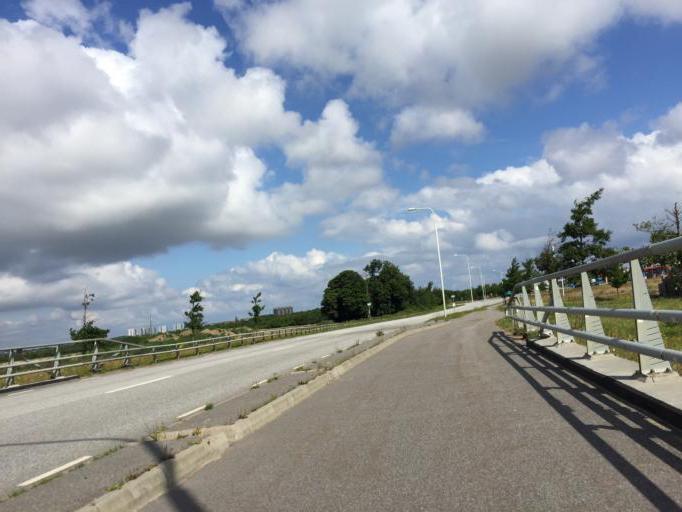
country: SE
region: Skane
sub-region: Malmo
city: Tygelsjo
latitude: 55.5458
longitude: 13.0337
